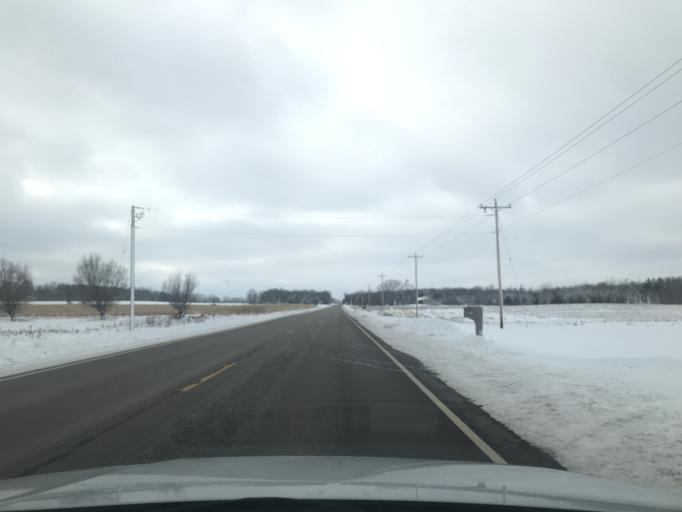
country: US
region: Wisconsin
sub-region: Oconto County
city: Oconto
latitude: 44.9503
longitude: -87.9817
